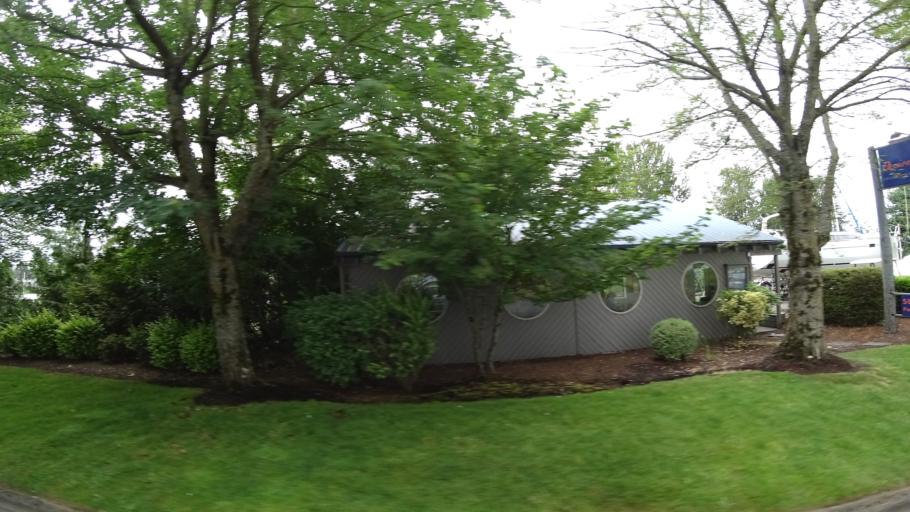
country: US
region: Washington
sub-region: Clark County
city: Vancouver
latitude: 45.6044
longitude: -122.6627
